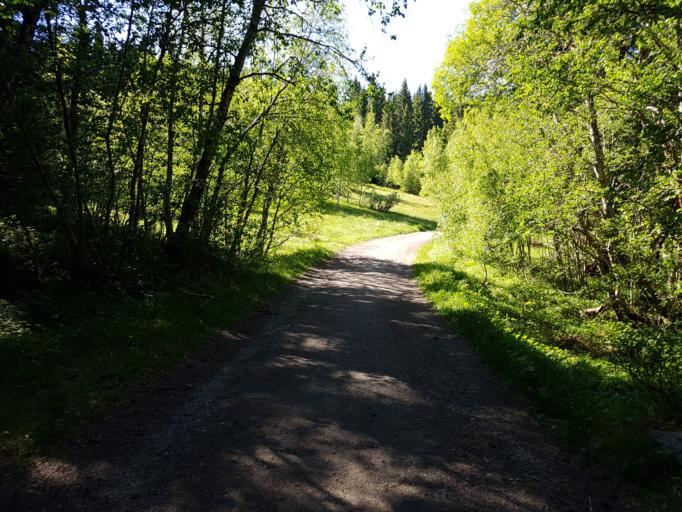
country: NO
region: Sor-Trondelag
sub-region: Trondheim
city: Trondheim
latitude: 63.4175
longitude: 10.3131
